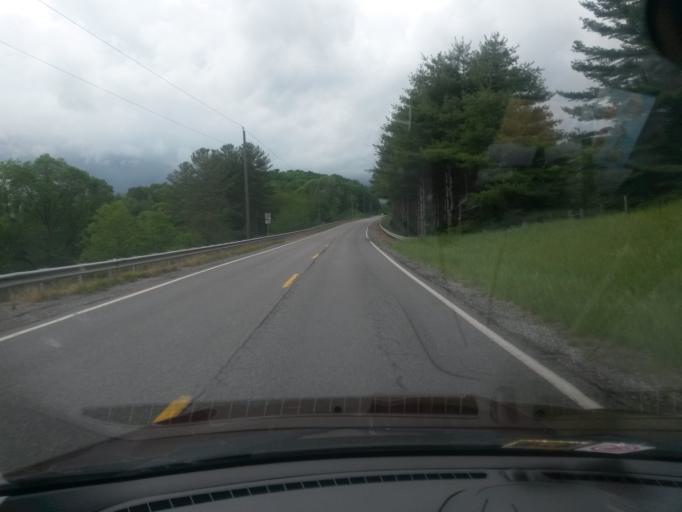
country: US
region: Virginia
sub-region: Floyd County
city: Floyd
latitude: 36.9406
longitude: -80.3482
